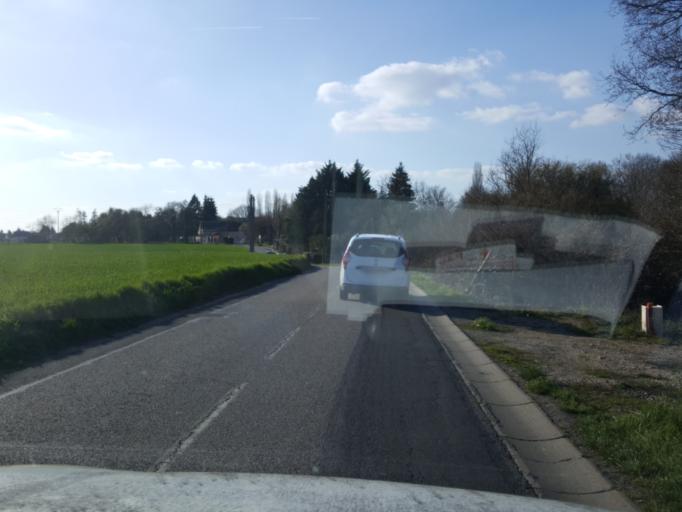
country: FR
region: Ile-de-France
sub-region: Departement des Yvelines
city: Gazeran
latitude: 48.6282
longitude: 1.7856
